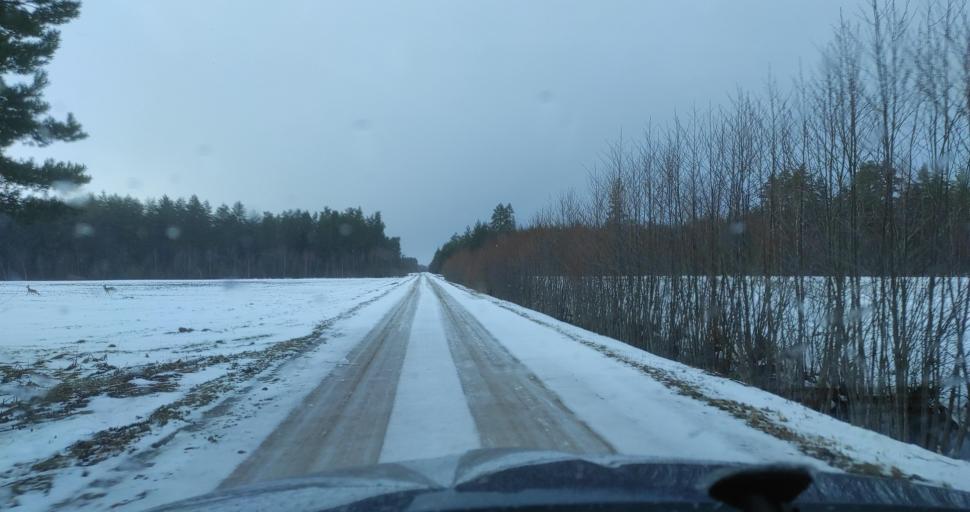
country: LV
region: Dundaga
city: Dundaga
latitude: 57.3788
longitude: 22.1612
